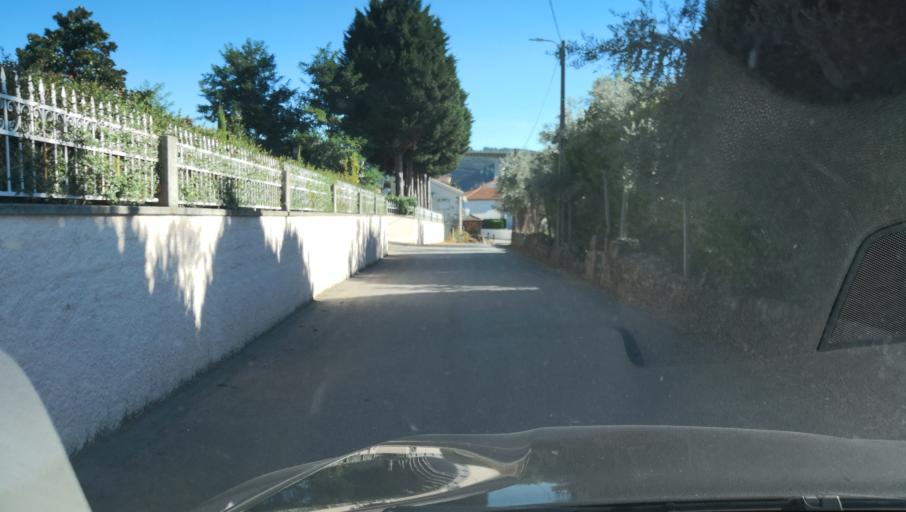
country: PT
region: Vila Real
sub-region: Vila Real
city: Vila Real
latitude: 41.2823
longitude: -7.7440
